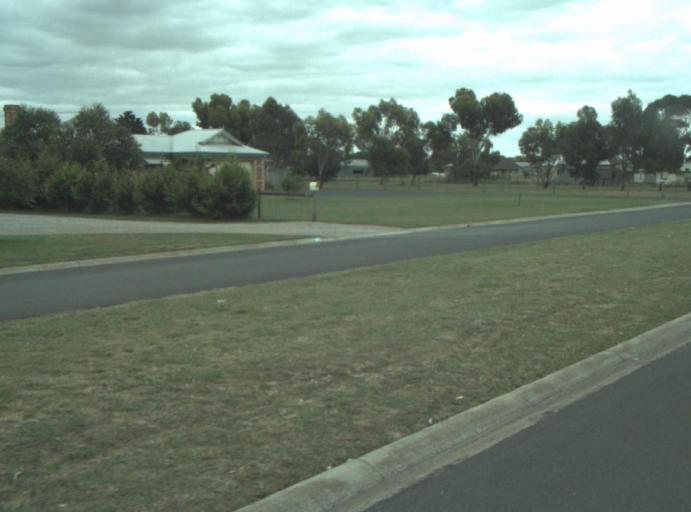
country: AU
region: Victoria
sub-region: Greater Geelong
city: Breakwater
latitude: -38.2168
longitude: 144.3383
